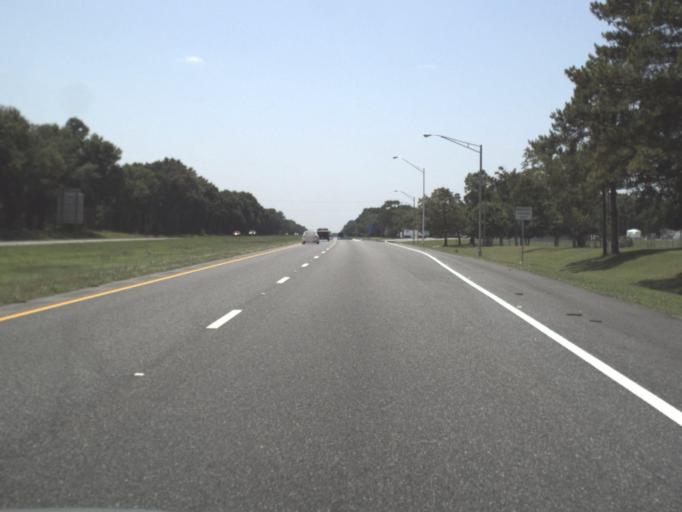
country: US
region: Florida
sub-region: Suwannee County
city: Wellborn
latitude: 30.2721
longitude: -82.7790
